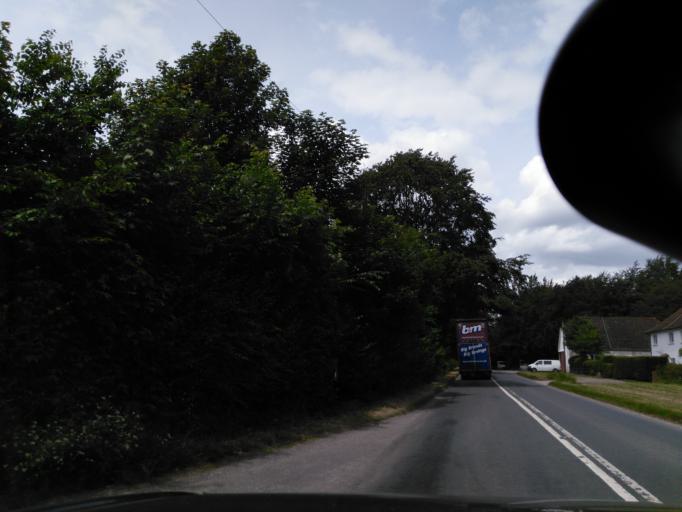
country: GB
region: England
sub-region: Wiltshire
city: Winterbourne Stoke
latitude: 51.1512
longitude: -1.8592
